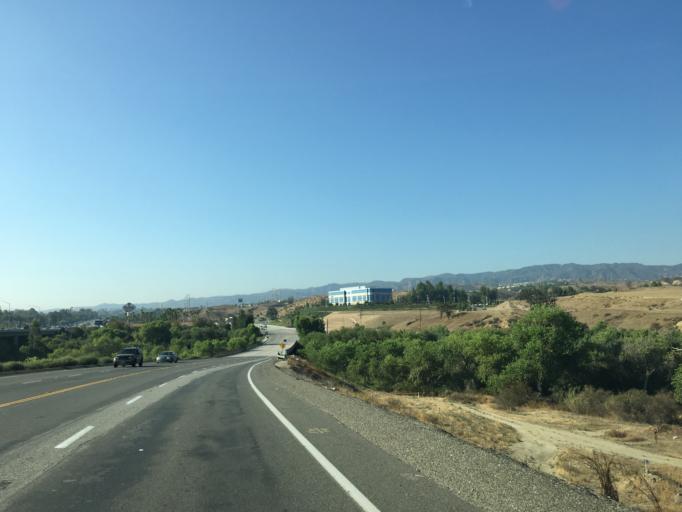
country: US
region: California
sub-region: Los Angeles County
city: Valencia
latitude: 34.4282
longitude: -118.5868
